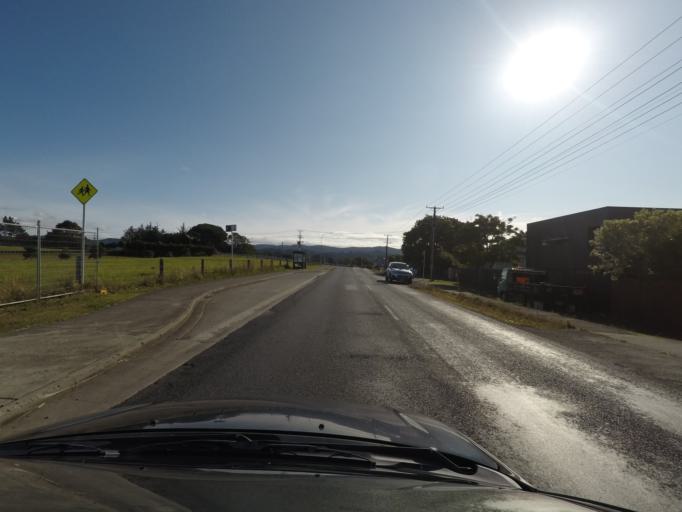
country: NZ
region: Auckland
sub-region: Auckland
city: Rosebank
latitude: -36.8744
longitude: 174.5981
